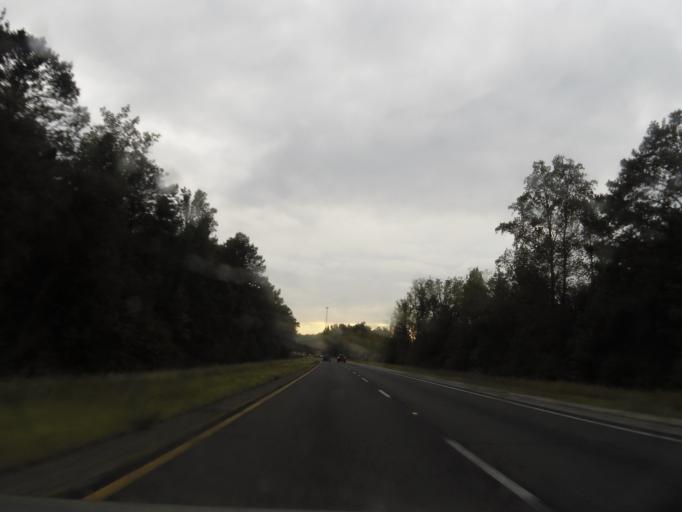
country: US
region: Alabama
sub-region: Saint Clair County
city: Springville
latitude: 33.7604
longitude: -86.4750
